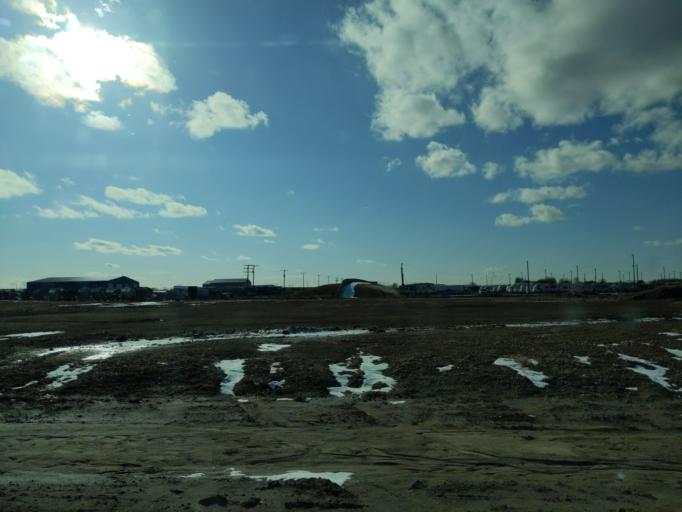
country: CA
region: Saskatchewan
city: Lloydminster
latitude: 53.2458
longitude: -109.9708
